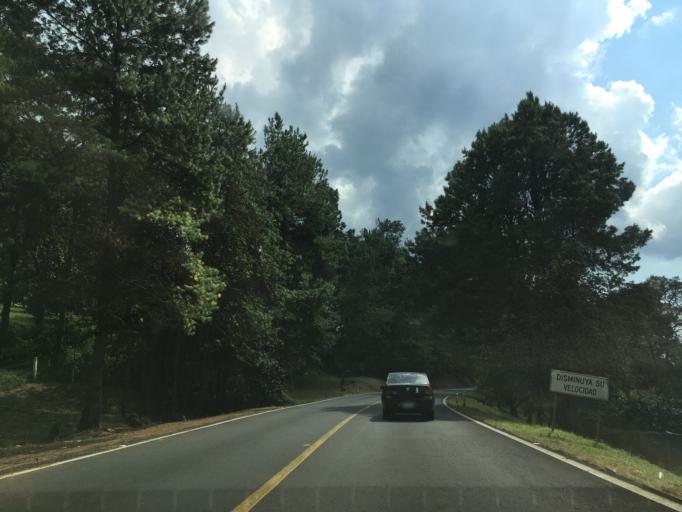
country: MX
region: Michoacan
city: Tingambato
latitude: 19.5016
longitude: -101.8353
